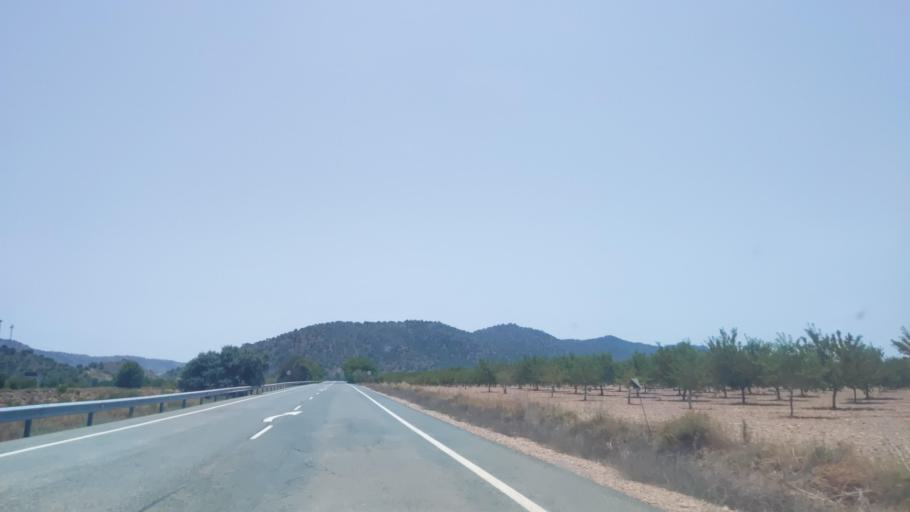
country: ES
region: Castille-La Mancha
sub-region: Provincia de Albacete
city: Tobarra
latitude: 38.6817
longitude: -1.6723
